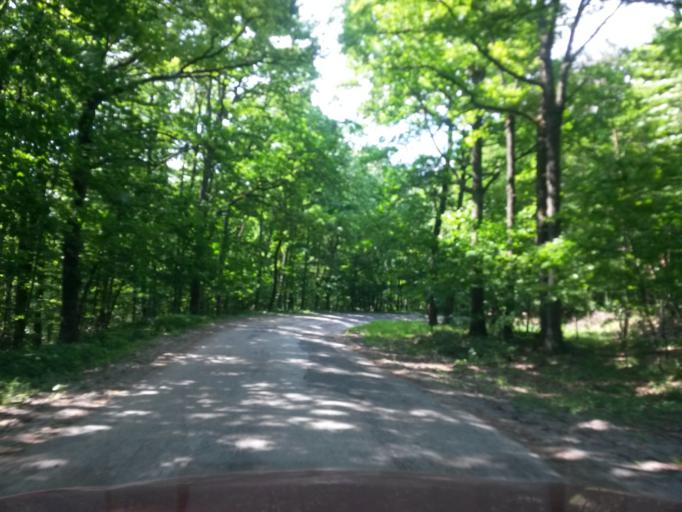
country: SK
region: Kosicky
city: Moldava nad Bodvou
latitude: 48.7170
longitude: 21.0285
